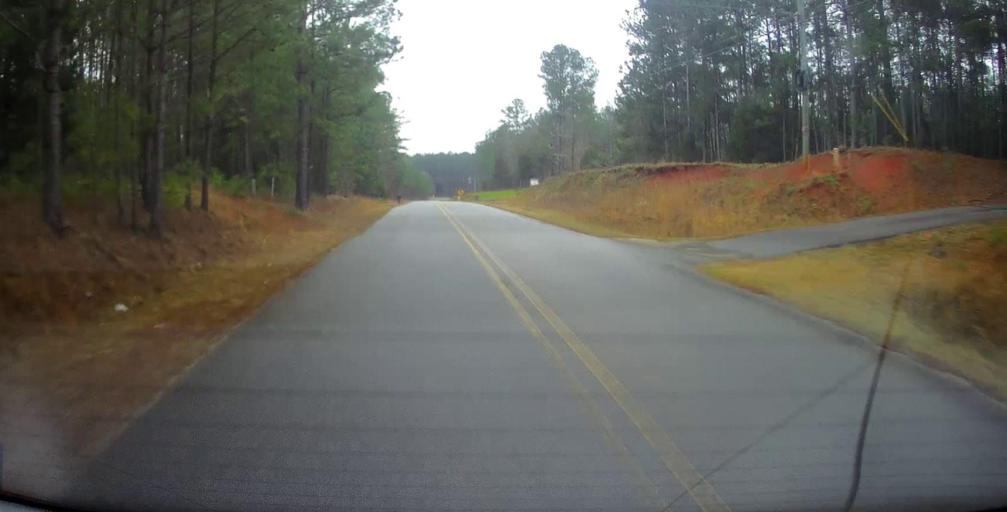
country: US
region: Georgia
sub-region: Monroe County
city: Forsyth
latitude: 33.0825
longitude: -83.9135
